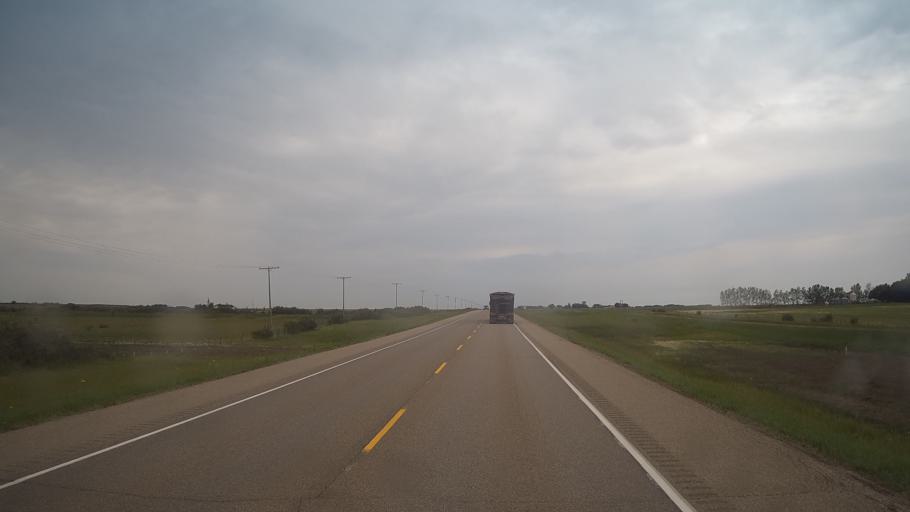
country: CA
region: Saskatchewan
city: Langham
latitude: 52.1288
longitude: -107.1749
